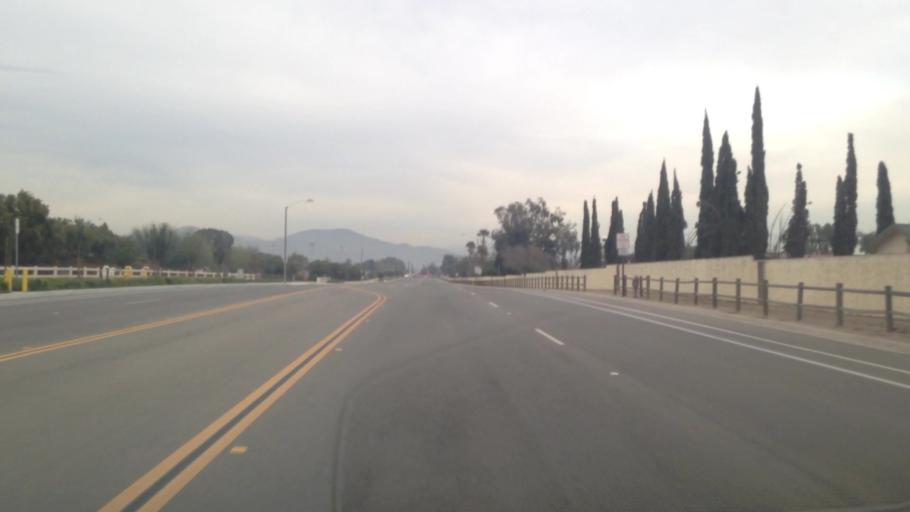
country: US
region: California
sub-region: Riverside County
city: Mira Loma
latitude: 33.9963
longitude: -117.5336
